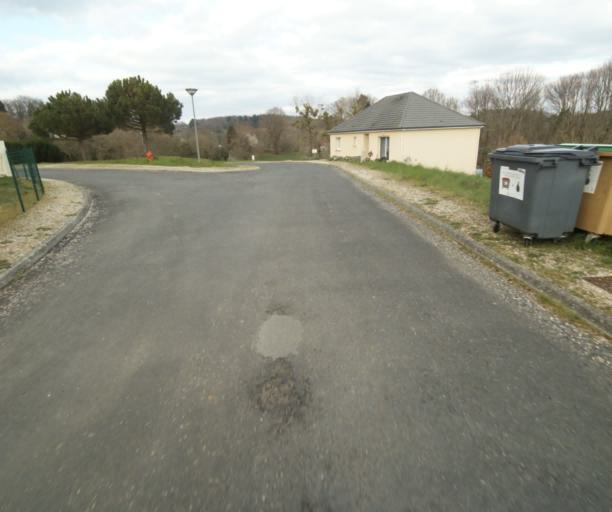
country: FR
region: Limousin
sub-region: Departement de la Correze
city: Saint-Clement
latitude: 45.3549
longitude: 1.6415
